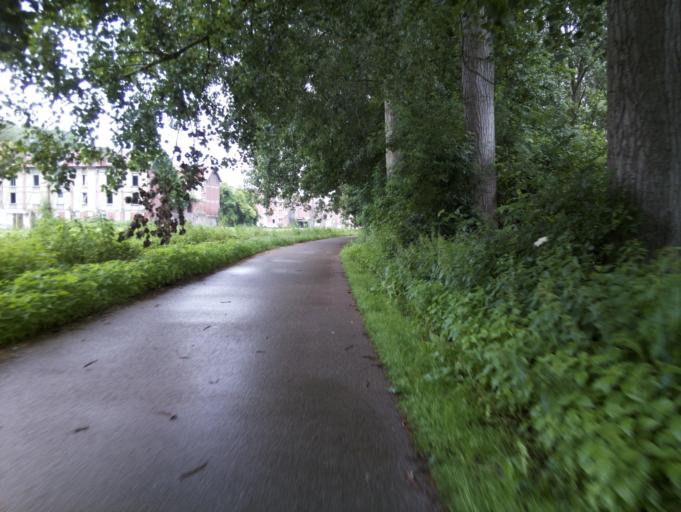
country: FR
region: Picardie
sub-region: Departement de la Somme
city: Saint-Sauveur
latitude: 49.9257
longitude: 2.2089
